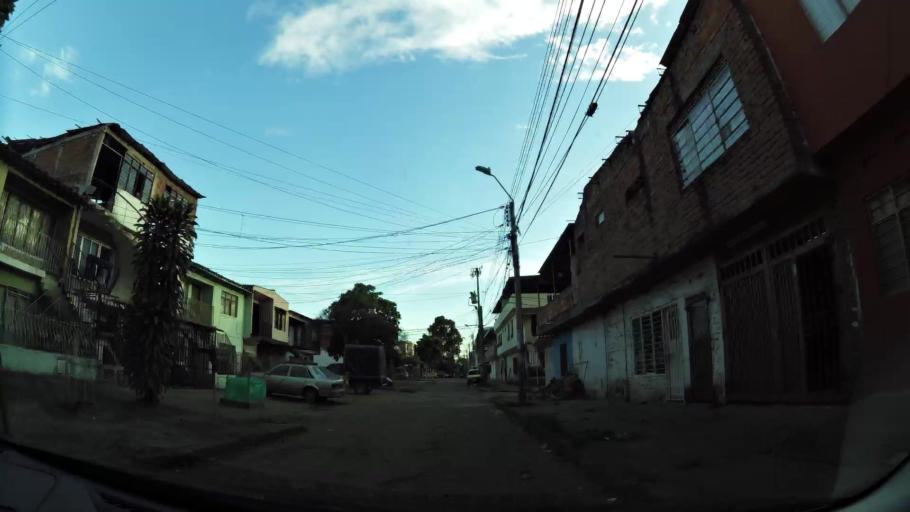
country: CO
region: Valle del Cauca
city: Cali
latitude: 3.4266
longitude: -76.5104
